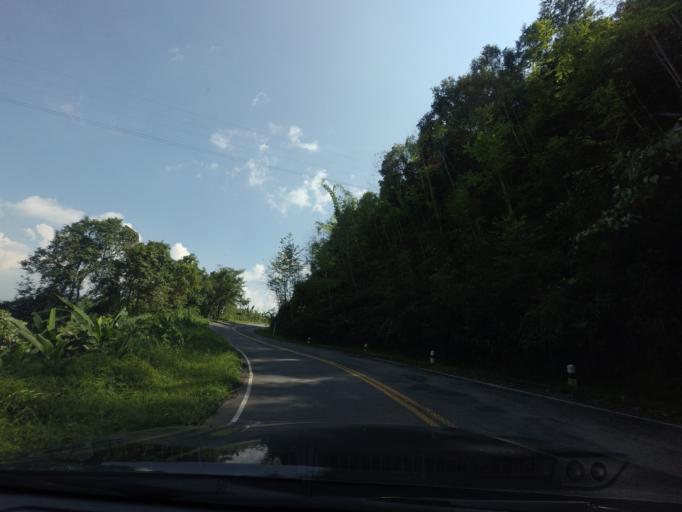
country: TH
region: Nan
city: Bo Kluea
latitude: 19.0573
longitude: 101.0877
